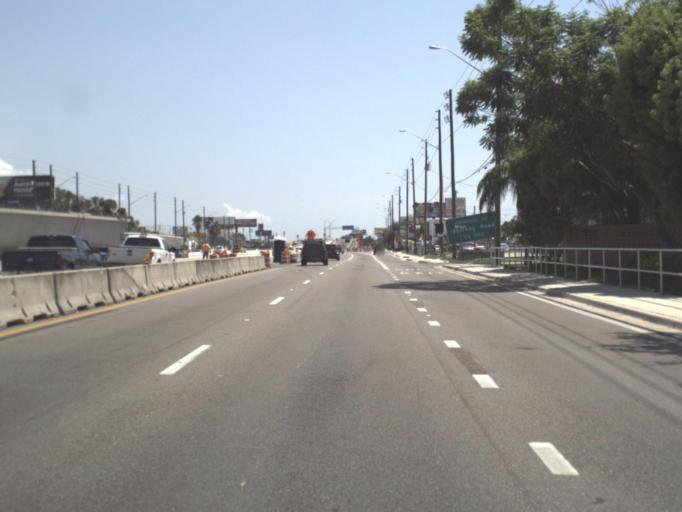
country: US
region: Florida
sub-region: Pinellas County
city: South Highpoint
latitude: 27.9299
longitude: -82.7306
